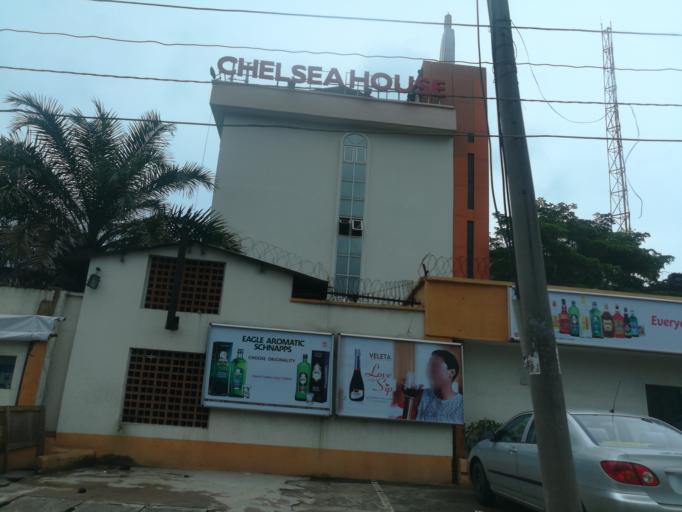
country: NG
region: Lagos
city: Agege
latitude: 6.6150
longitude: 3.3420
